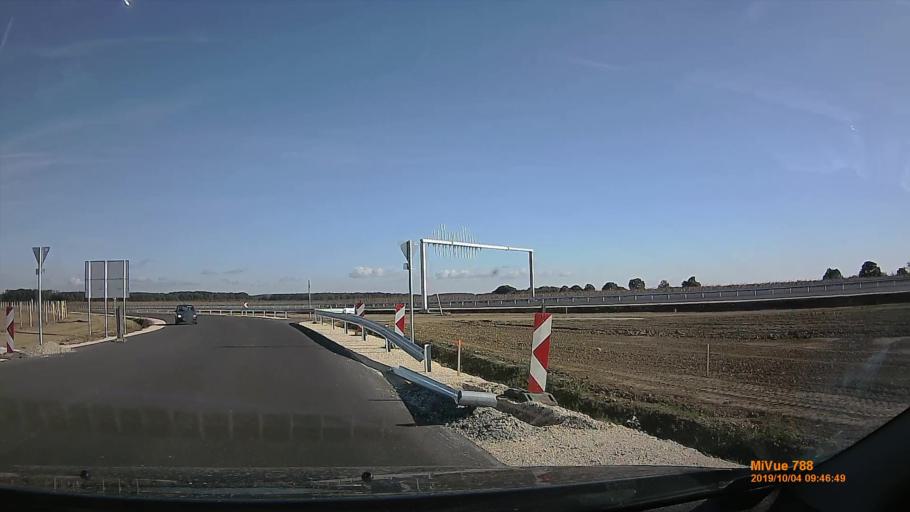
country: HU
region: Somogy
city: Kaposvar
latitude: 46.4255
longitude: 17.7743
